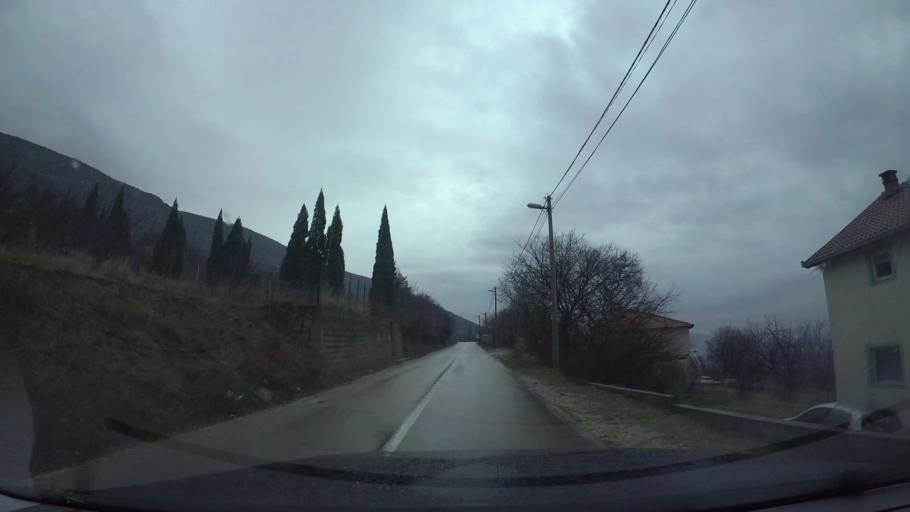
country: BA
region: Federation of Bosnia and Herzegovina
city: Rodoc
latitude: 43.3040
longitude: 17.8515
